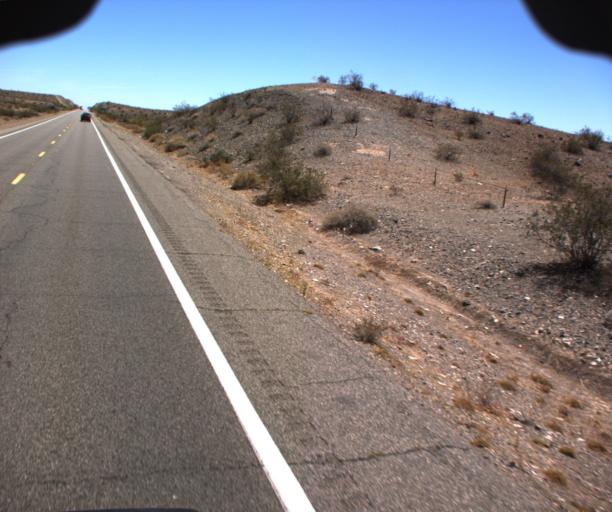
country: US
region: Arizona
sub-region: Mohave County
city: Lake Havasu City
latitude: 34.4356
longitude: -114.2218
